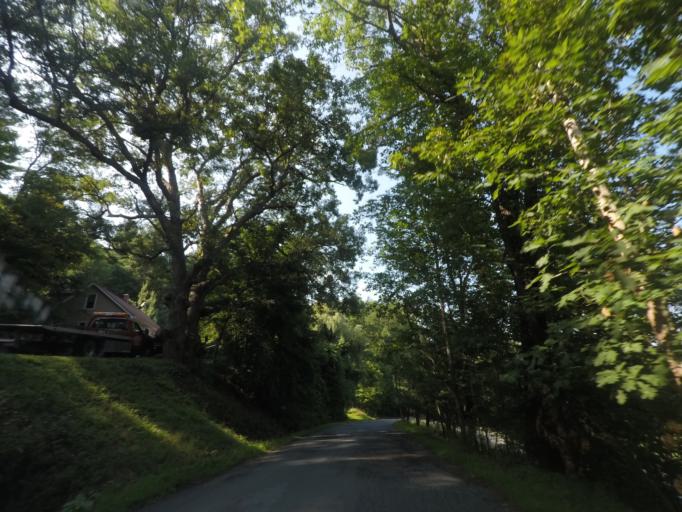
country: US
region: New York
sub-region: Rensselaer County
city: Nassau
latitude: 42.5228
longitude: -73.5672
